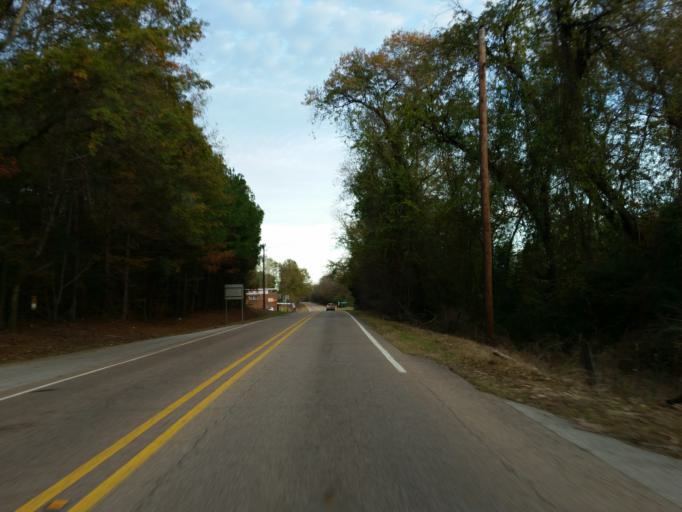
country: US
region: Alabama
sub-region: Sumter County
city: York
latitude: 32.4243
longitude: -88.4404
